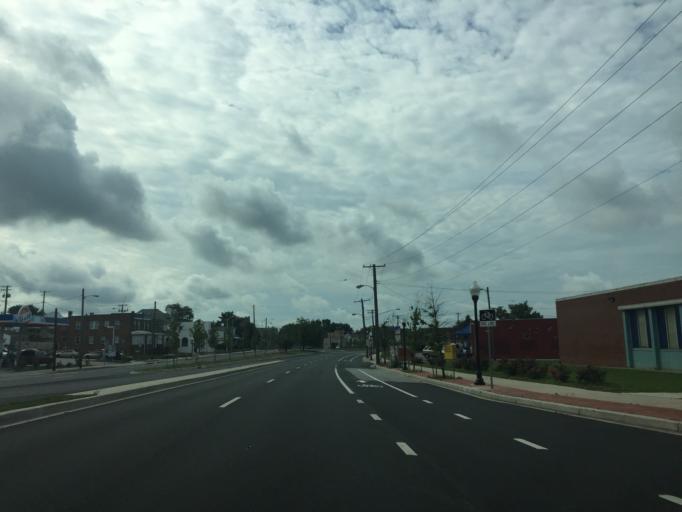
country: US
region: Maryland
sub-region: Baltimore County
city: Dundalk
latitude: 39.2831
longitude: -76.5370
